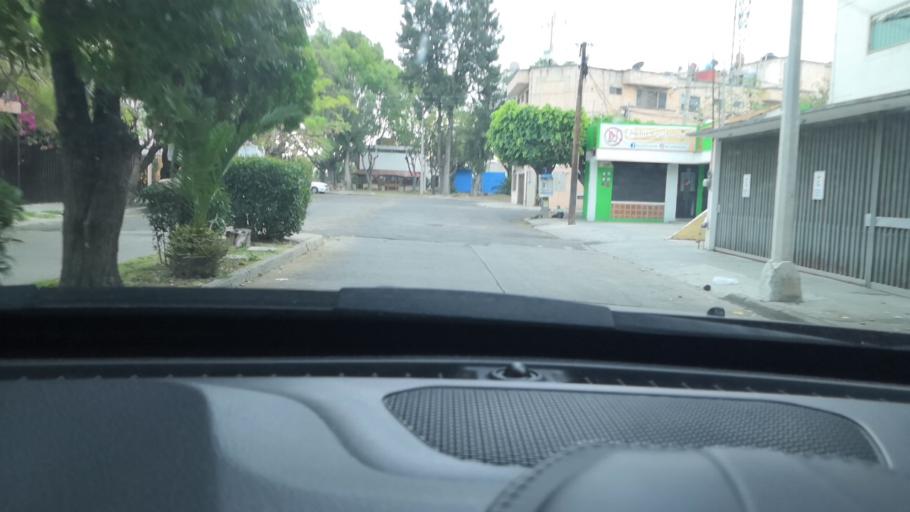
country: MX
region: Guanajuato
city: Leon
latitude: 21.1107
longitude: -101.6681
